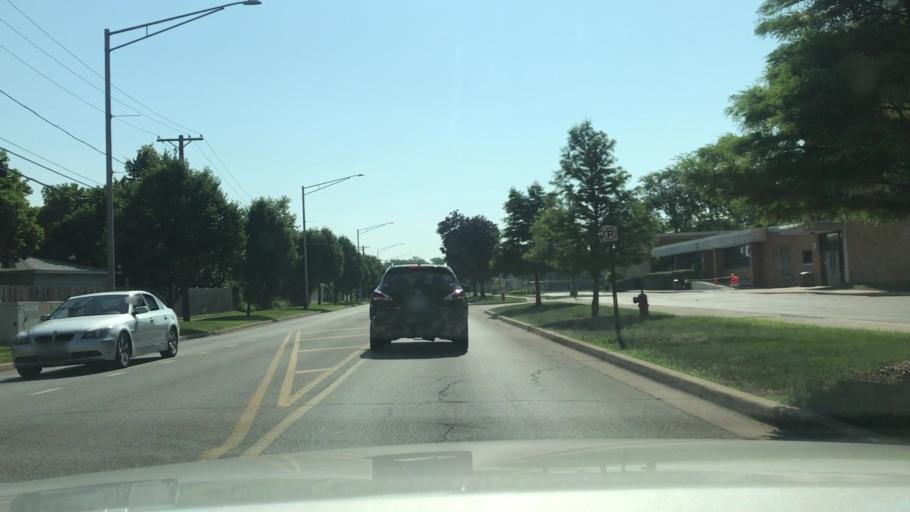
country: US
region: Illinois
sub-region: Cook County
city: Evergreen Park
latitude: 41.7134
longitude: -87.7011
